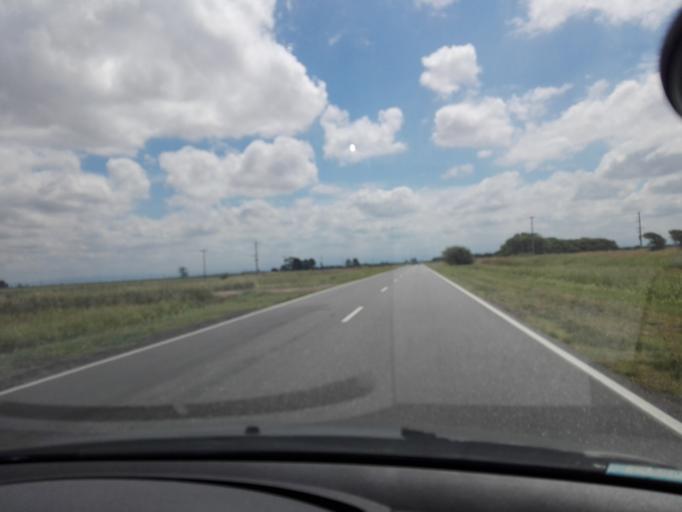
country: AR
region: Cordoba
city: Toledo
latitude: -31.6464
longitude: -64.0493
